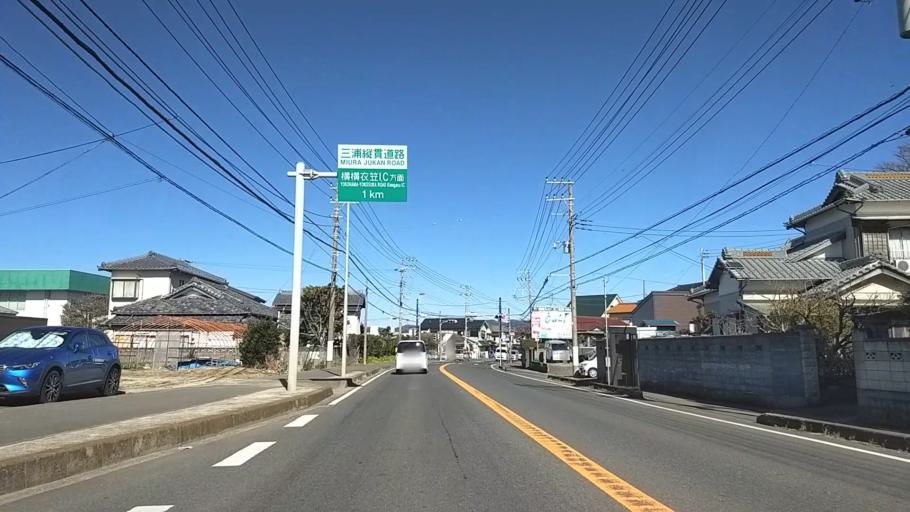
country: JP
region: Kanagawa
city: Miura
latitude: 35.2026
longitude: 139.6257
